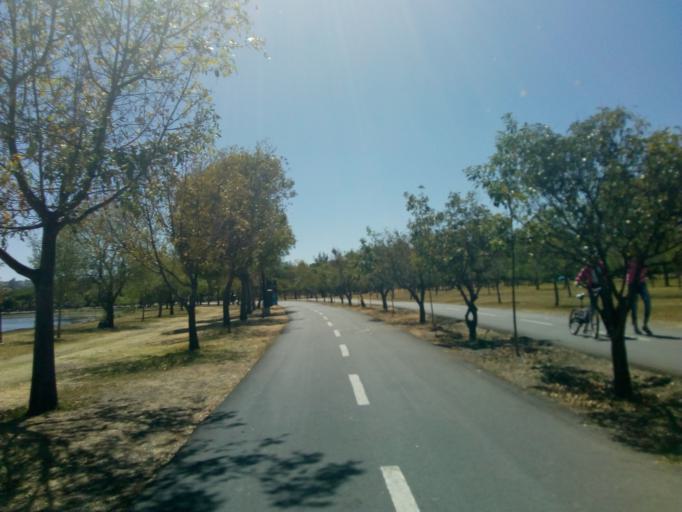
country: MX
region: Guanajuato
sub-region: Leon
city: La Ermita
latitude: 21.1864
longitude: -101.6925
